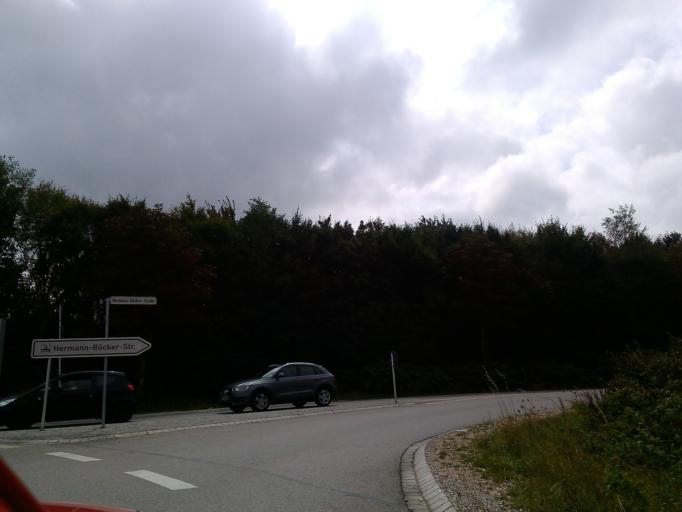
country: DE
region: Bavaria
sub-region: Upper Bavaria
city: Olching
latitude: 48.2235
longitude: 11.3346
